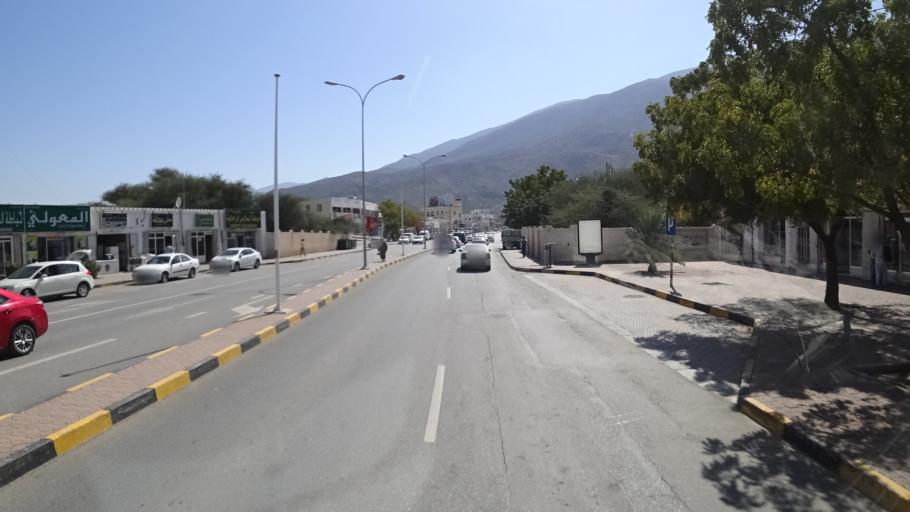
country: OM
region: Al Batinah
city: Rustaq
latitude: 23.3943
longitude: 57.4224
